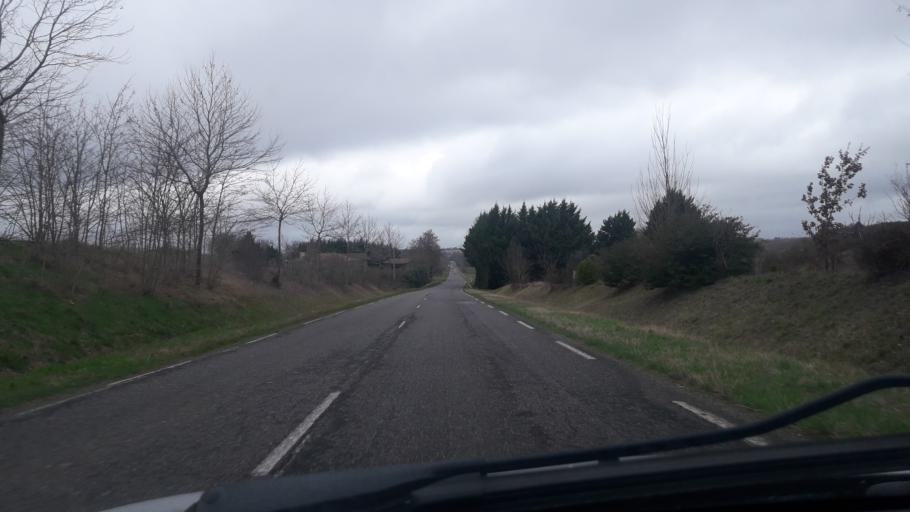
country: FR
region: Midi-Pyrenees
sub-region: Departement du Gers
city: Gimont
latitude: 43.6700
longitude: 1.0149
